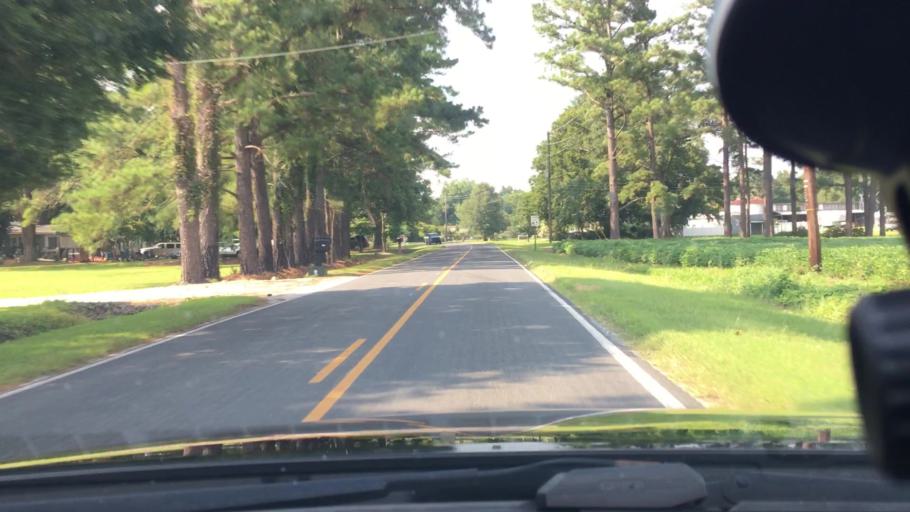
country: US
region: North Carolina
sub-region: Craven County
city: New Bern
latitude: 35.1721
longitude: -77.0511
